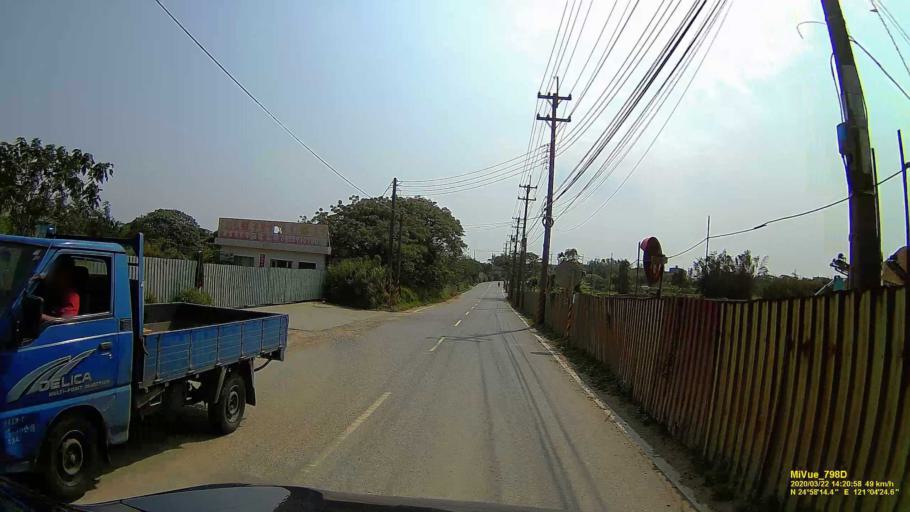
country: TW
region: Taiwan
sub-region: Hsinchu
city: Zhubei
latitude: 24.9705
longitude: 121.0733
